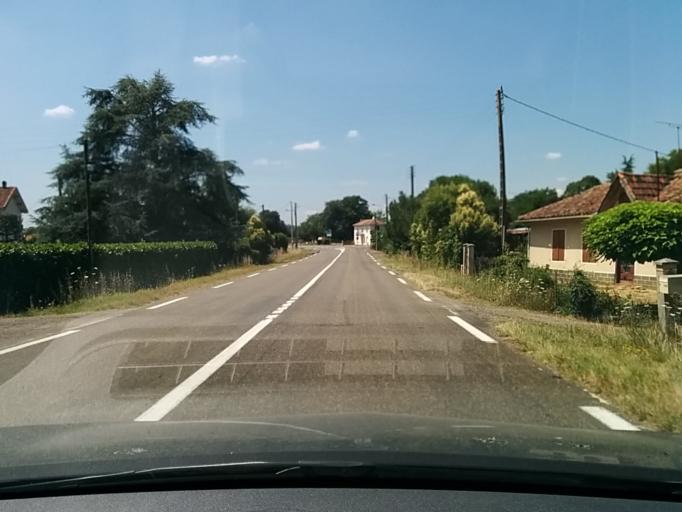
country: FR
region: Midi-Pyrenees
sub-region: Departement du Gers
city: Eauze
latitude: 43.8003
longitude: 0.0481
